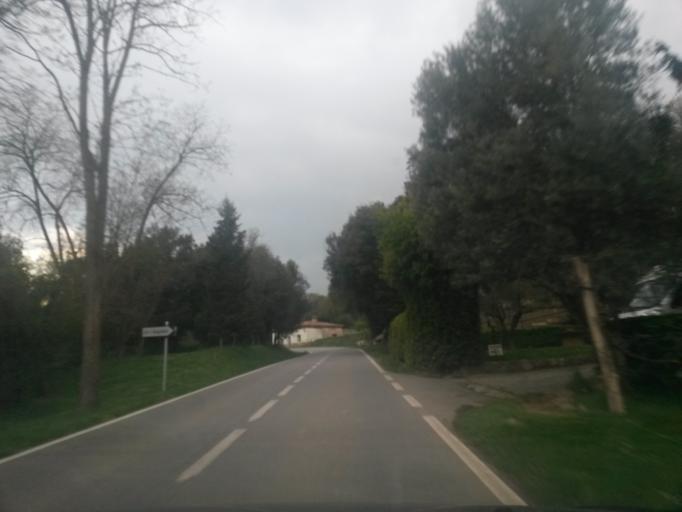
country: ES
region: Catalonia
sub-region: Provincia de Barcelona
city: Sagas
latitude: 42.0385
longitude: 1.9701
